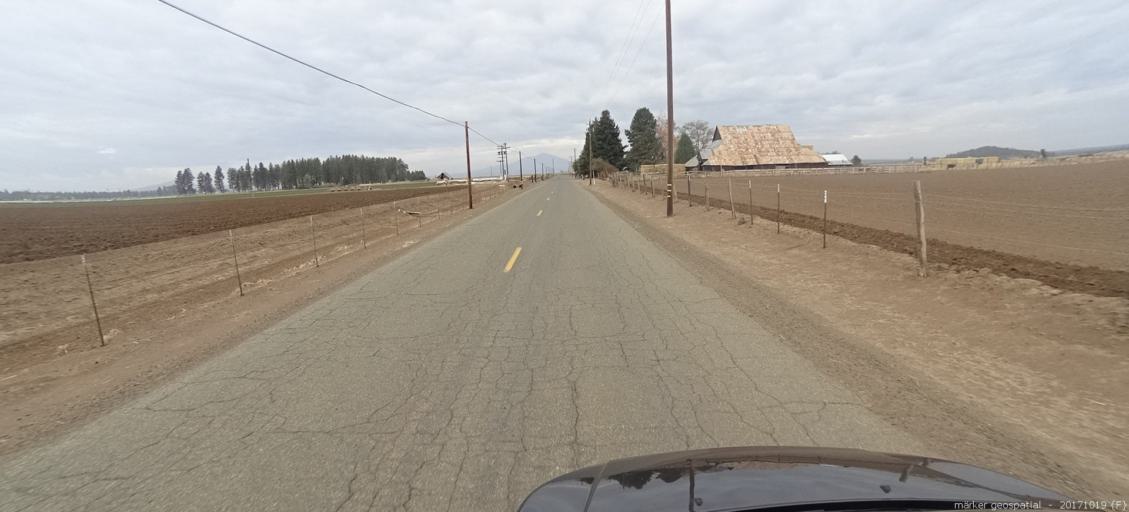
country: US
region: California
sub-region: Shasta County
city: Burney
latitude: 41.0805
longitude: -121.3442
